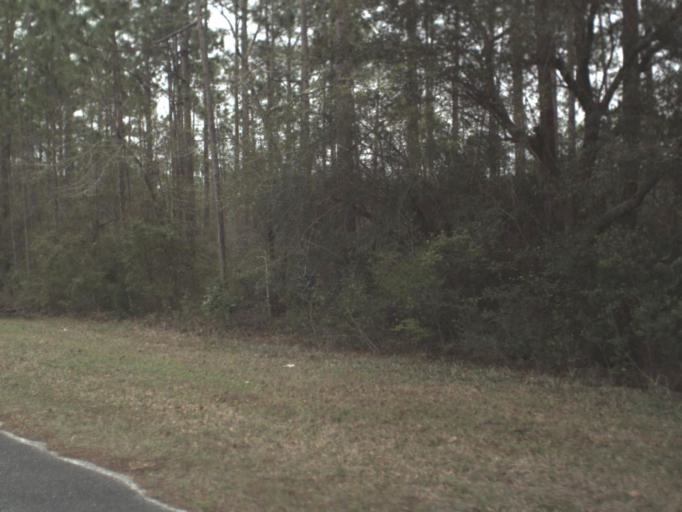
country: US
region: Florida
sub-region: Franklin County
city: Eastpoint
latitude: 29.8292
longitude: -84.8831
